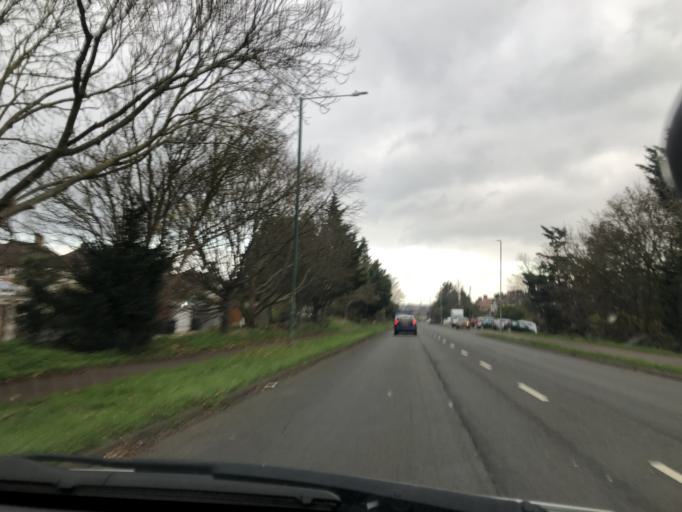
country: GB
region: England
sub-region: Kent
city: Dartford
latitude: 51.4462
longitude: 0.1919
